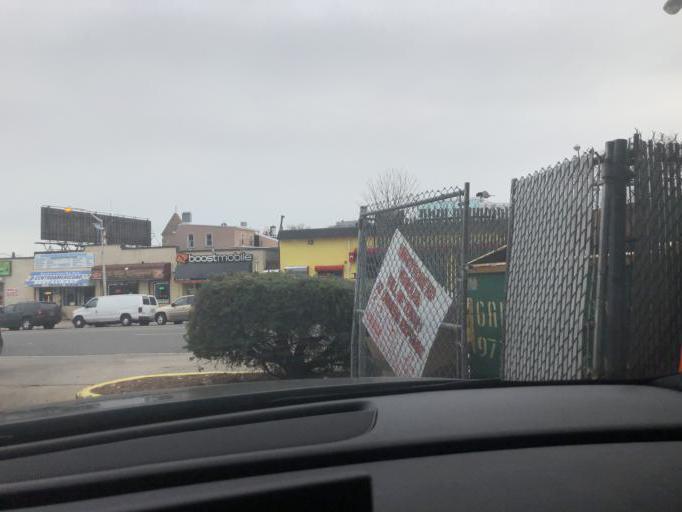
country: US
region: New Jersey
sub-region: Hudson County
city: East Newark
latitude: 40.7555
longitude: -74.1731
